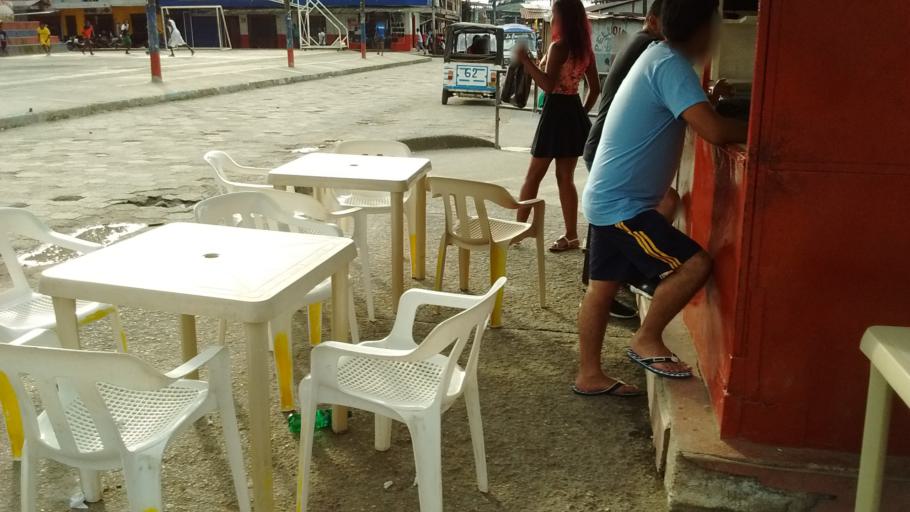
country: CO
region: Cauca
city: Guapi
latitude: 2.5708
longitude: -77.8821
